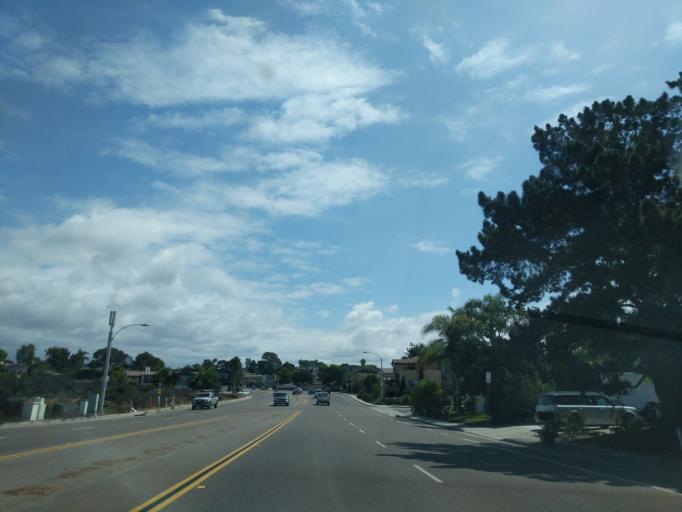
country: US
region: California
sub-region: San Diego County
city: Del Mar
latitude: 32.9493
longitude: -117.2549
